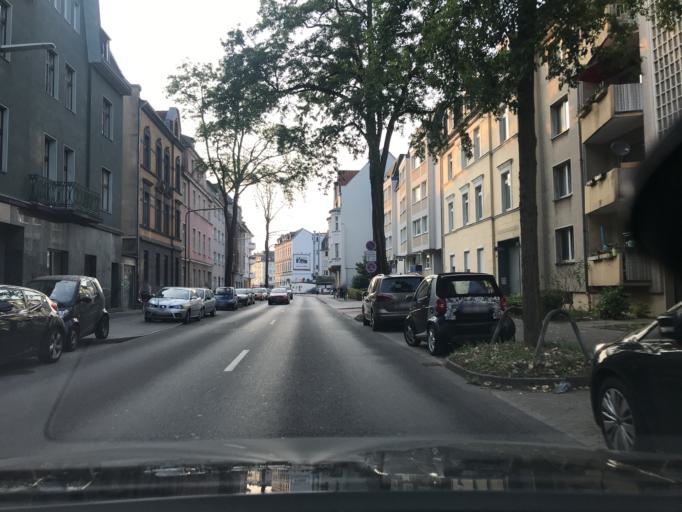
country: DE
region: North Rhine-Westphalia
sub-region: Regierungsbezirk Dusseldorf
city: Ratingen
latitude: 51.2610
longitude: 6.8130
